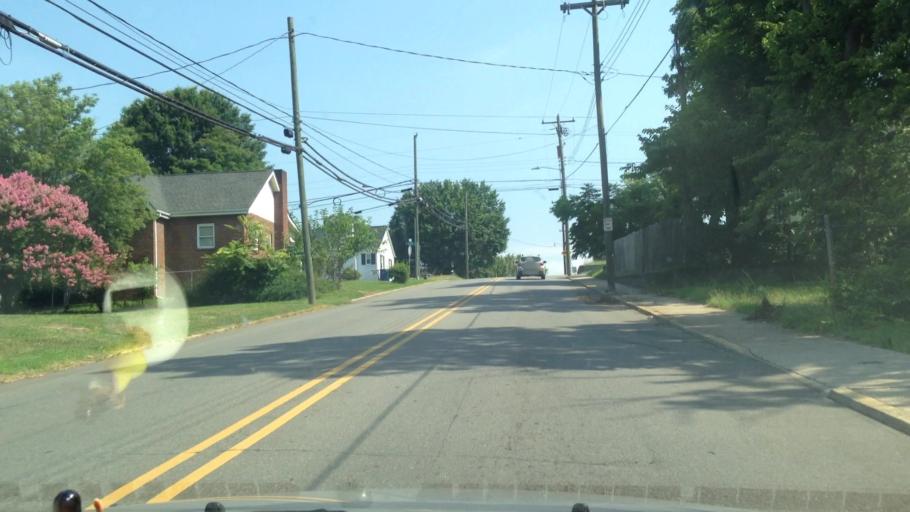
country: US
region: North Carolina
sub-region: Surry County
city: Mount Airy
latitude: 36.4904
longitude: -80.6108
